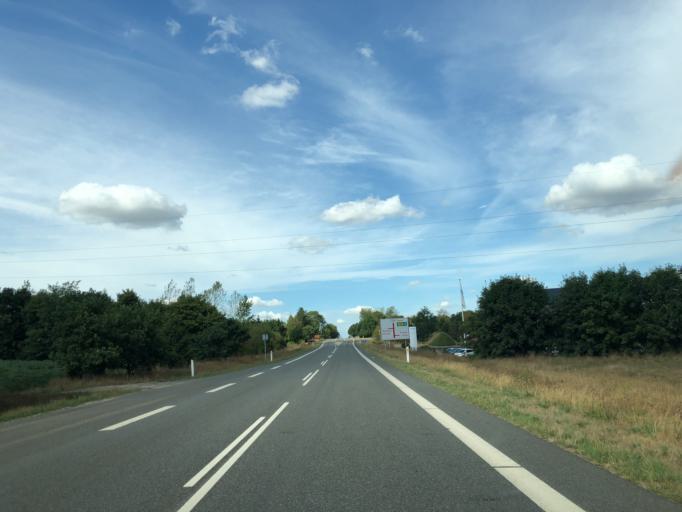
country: DK
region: Central Jutland
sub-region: Ikast-Brande Kommune
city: Bording Kirkeby
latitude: 56.1396
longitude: 9.2952
